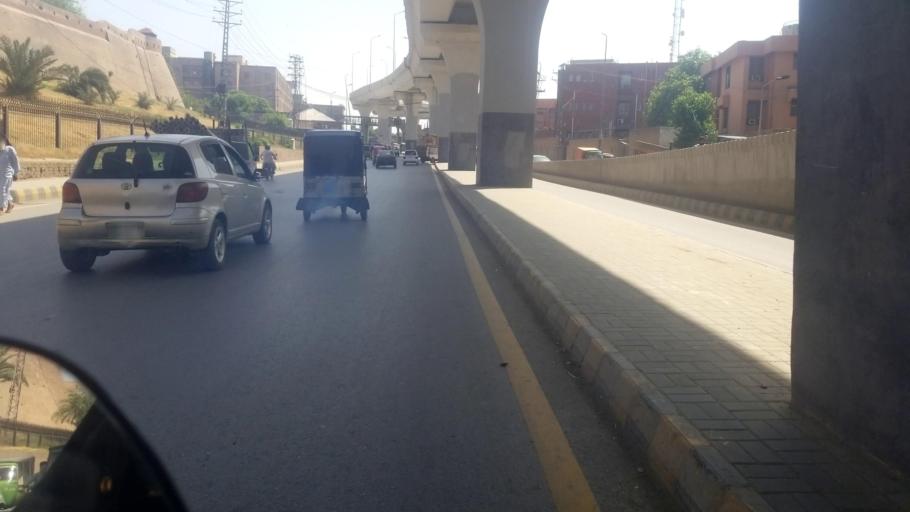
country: PK
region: Khyber Pakhtunkhwa
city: Peshawar
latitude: 34.0129
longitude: 71.5682
